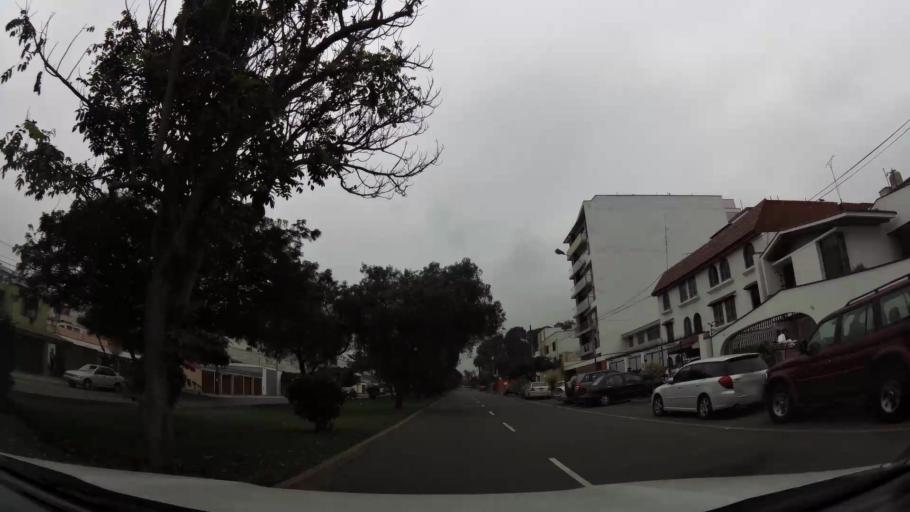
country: PE
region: Lima
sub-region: Lima
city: San Luis
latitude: -12.1049
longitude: -77.0158
